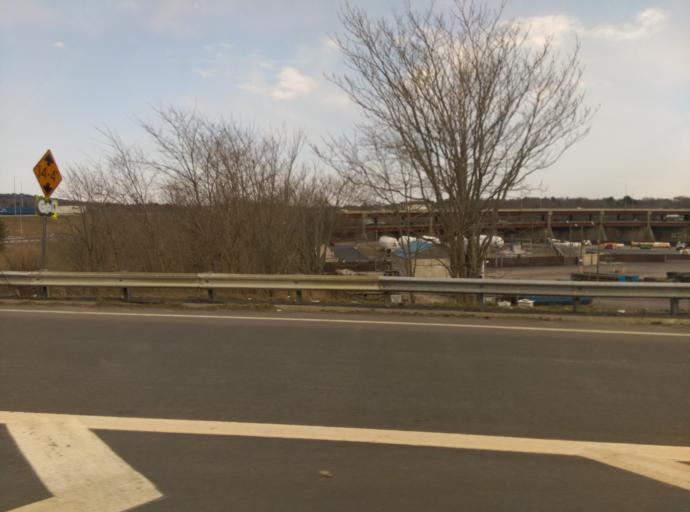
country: US
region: Massachusetts
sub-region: Essex County
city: North Andover
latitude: 42.7091
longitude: -71.1411
